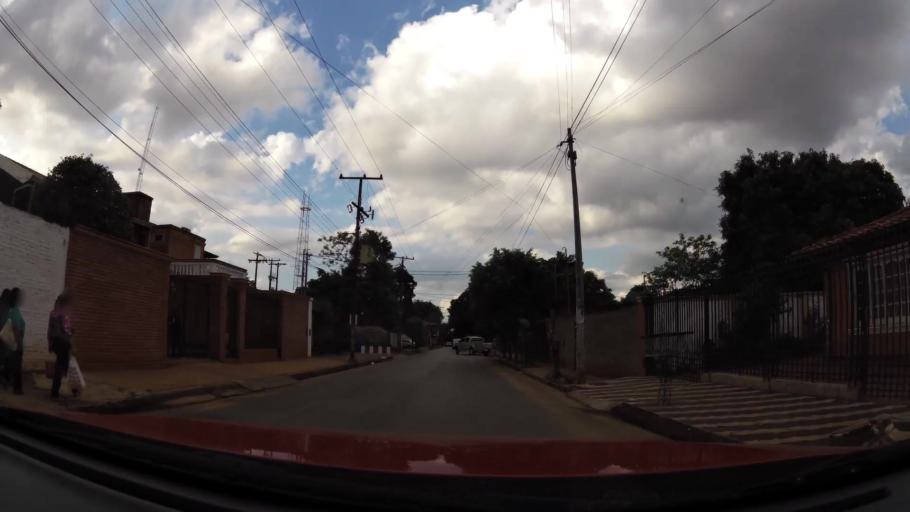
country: PY
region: Central
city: Fernando de la Mora
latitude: -25.3369
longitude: -57.5449
